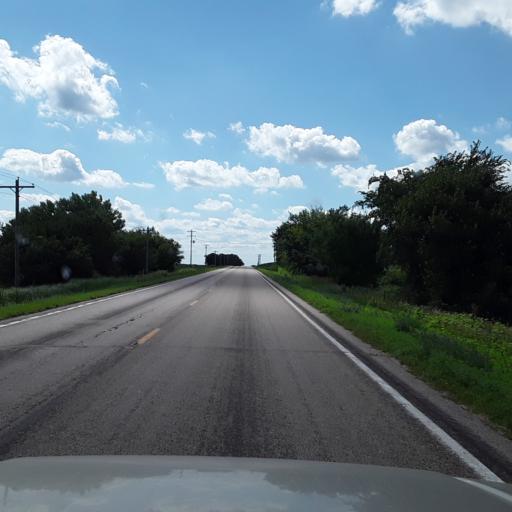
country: US
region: Nebraska
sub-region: Merrick County
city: Central City
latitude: 41.1910
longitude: -98.0141
